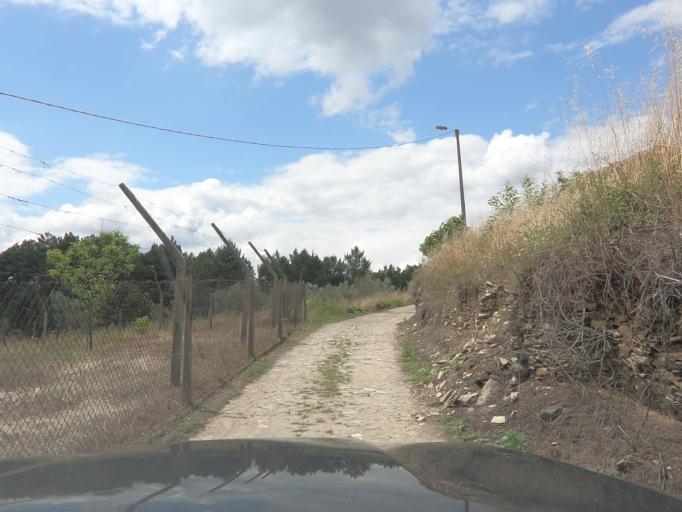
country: PT
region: Vila Real
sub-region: Sabrosa
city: Vilela
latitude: 41.2523
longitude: -7.6677
